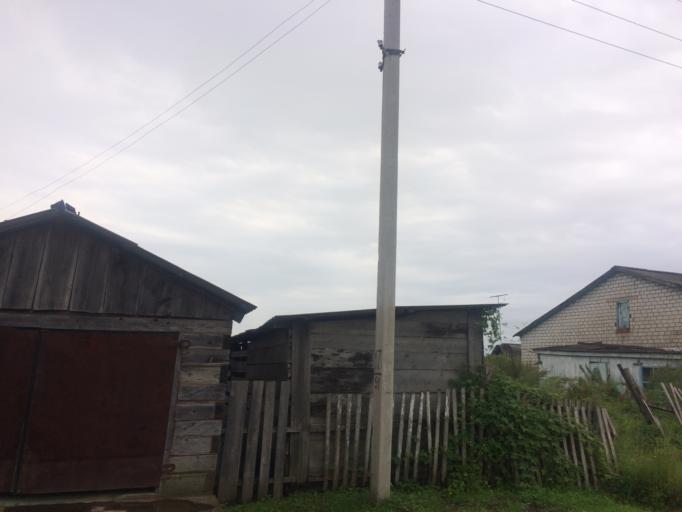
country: RU
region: Primorskiy
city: Lazo
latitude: 45.8279
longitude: 133.6132
